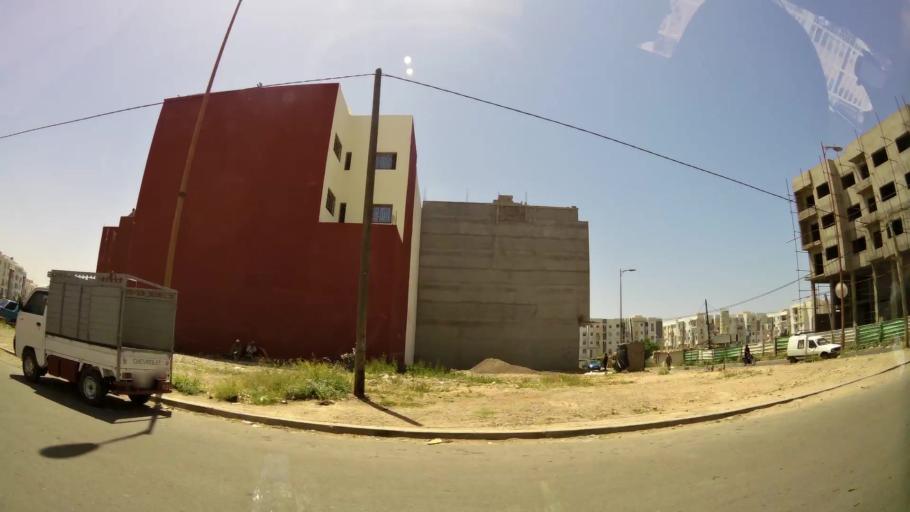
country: MA
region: Oued ed Dahab-Lagouira
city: Dakhla
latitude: 30.4373
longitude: -9.5567
